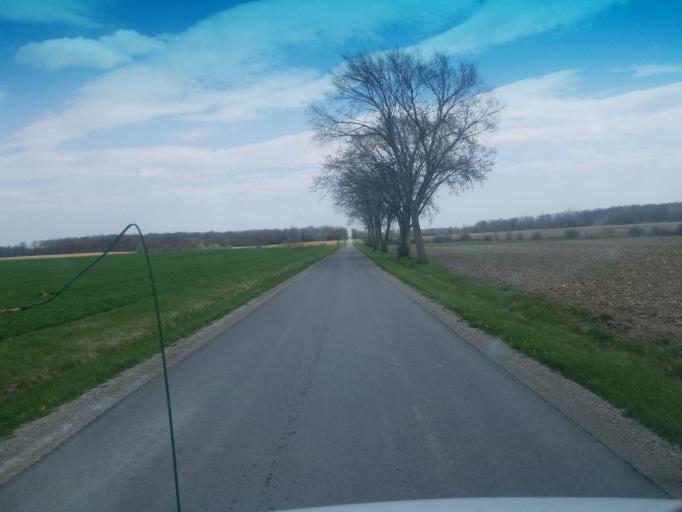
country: US
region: Ohio
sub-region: Hardin County
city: Forest
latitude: 40.7740
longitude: -83.4194
